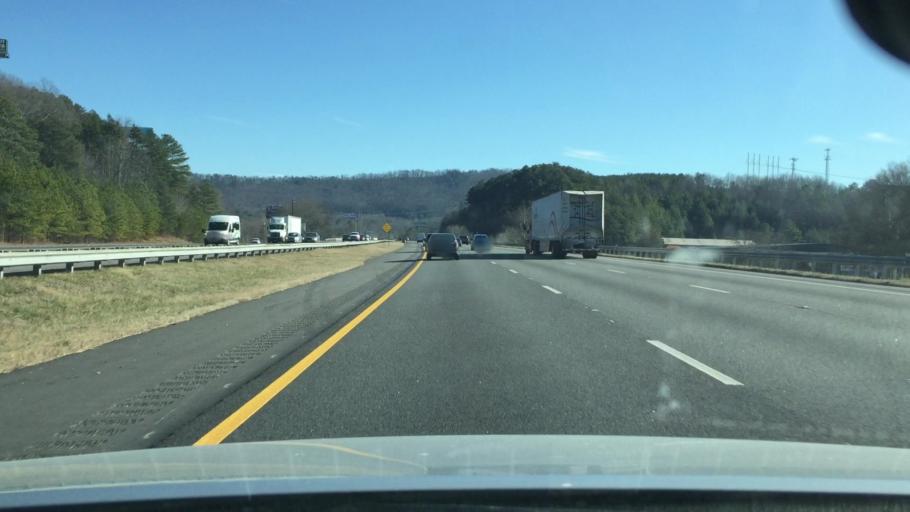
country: US
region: Georgia
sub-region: Whitfield County
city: Varnell
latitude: 34.8624
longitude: -85.0286
